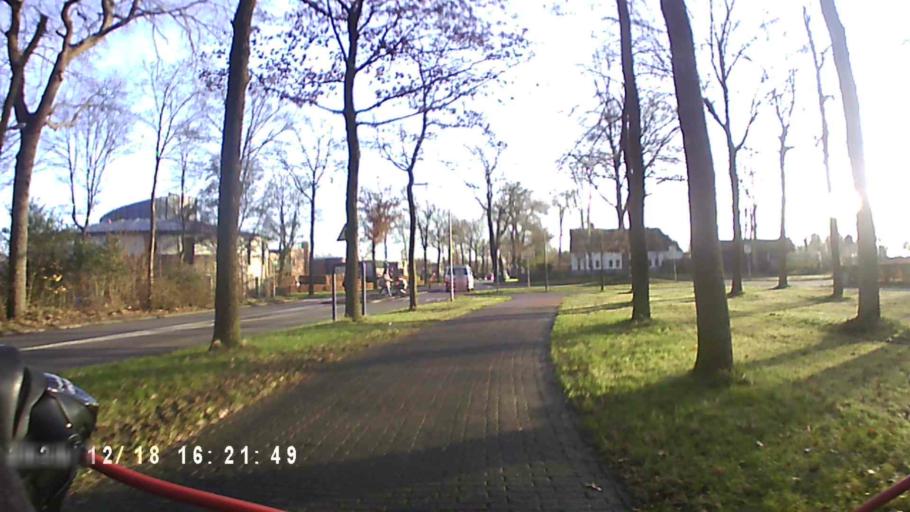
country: NL
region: Drenthe
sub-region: Gemeente Tynaarlo
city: Zuidlaren
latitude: 53.0917
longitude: 6.6904
